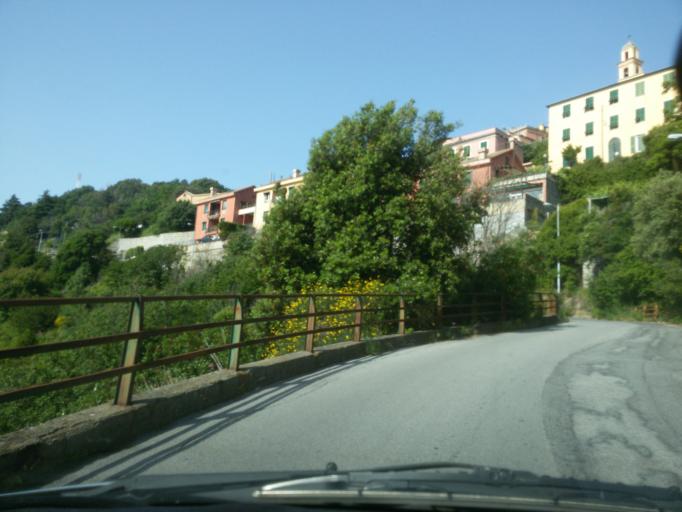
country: IT
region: Liguria
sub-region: Provincia di Genova
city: Genoa
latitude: 44.4269
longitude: 8.9132
